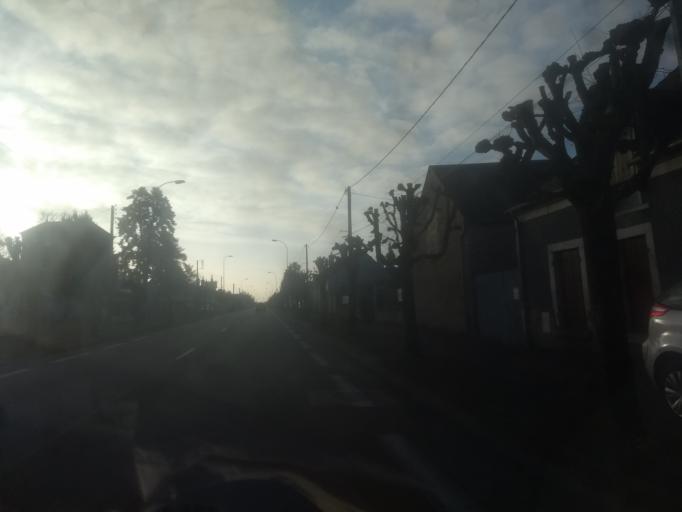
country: FR
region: Centre
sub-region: Departement du Cher
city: Mehun-sur-Yevre
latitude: 47.1517
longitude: 2.2140
